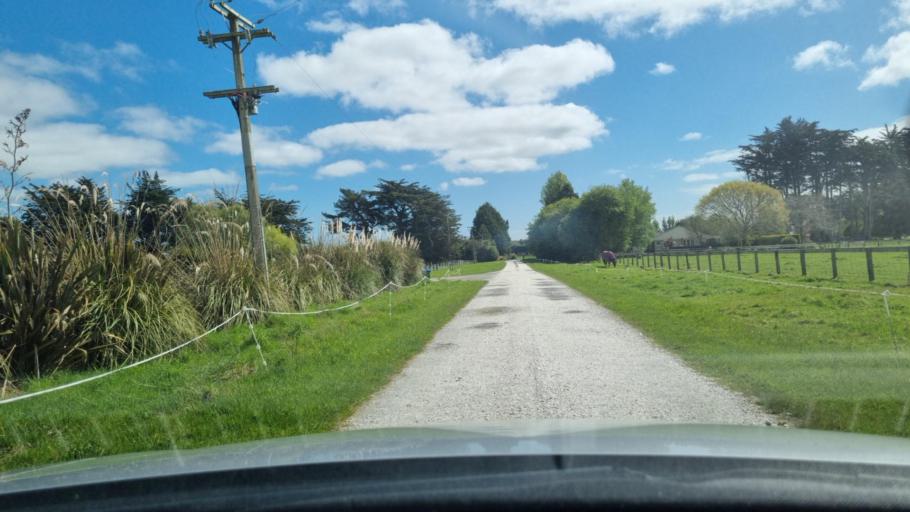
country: NZ
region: Southland
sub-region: Invercargill City
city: Invercargill
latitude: -46.3781
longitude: 168.4452
